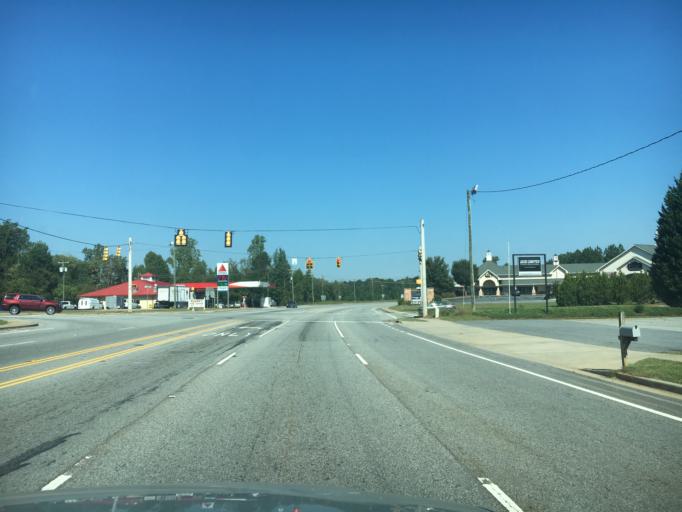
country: US
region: South Carolina
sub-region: Spartanburg County
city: Inman
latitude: 35.0906
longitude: -82.0385
